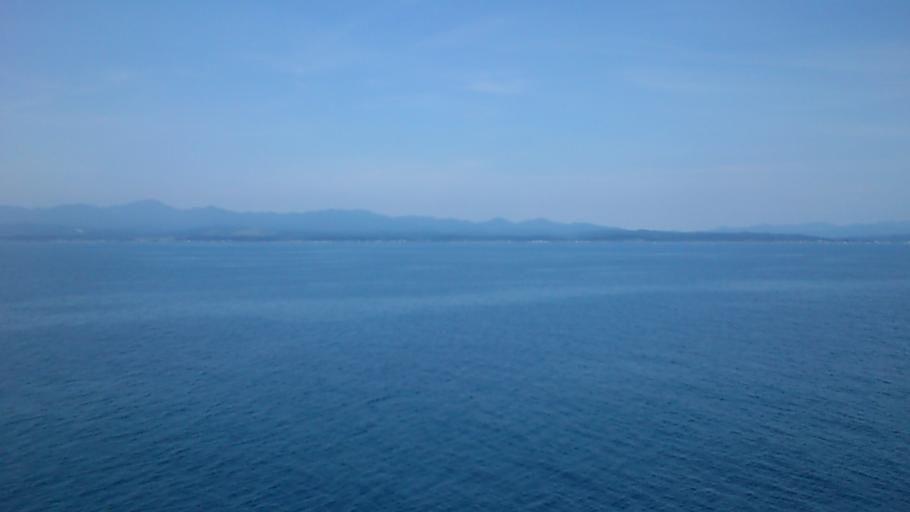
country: JP
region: Aomori
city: Aomori Shi
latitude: 41.0073
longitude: 140.7246
